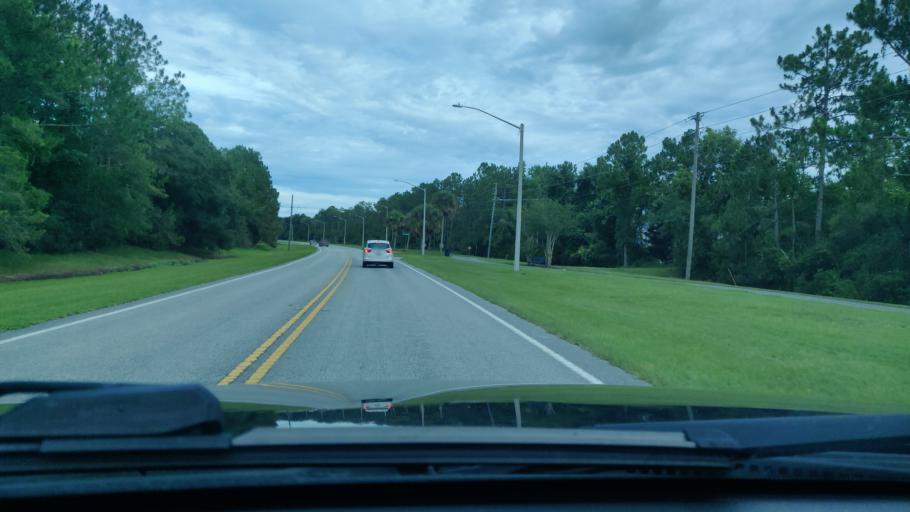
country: US
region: Florida
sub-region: Flagler County
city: Bunnell
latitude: 29.5319
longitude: -81.2524
